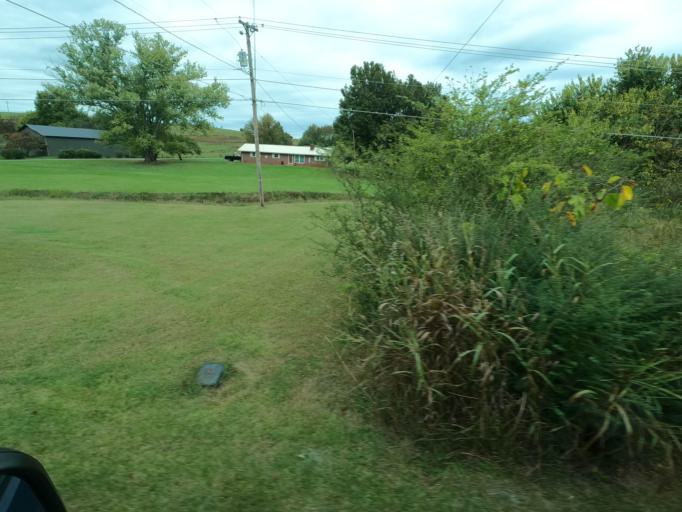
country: US
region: Tennessee
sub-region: Washington County
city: Jonesborough
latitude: 36.2214
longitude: -82.5760
